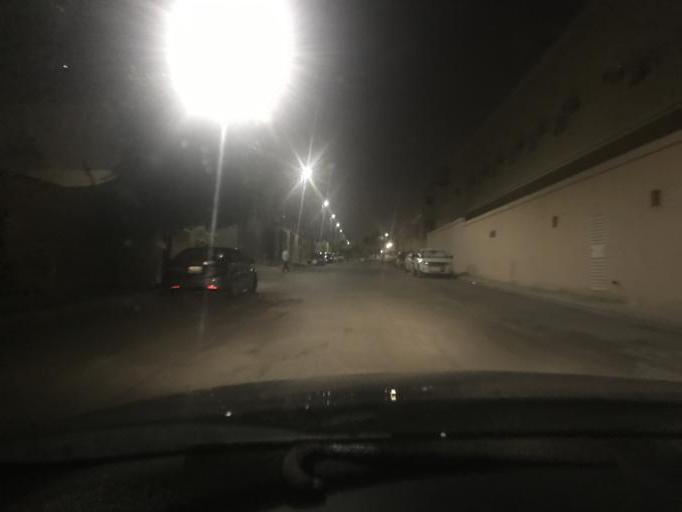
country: SA
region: Ar Riyad
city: Riyadh
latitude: 24.7266
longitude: 46.7651
